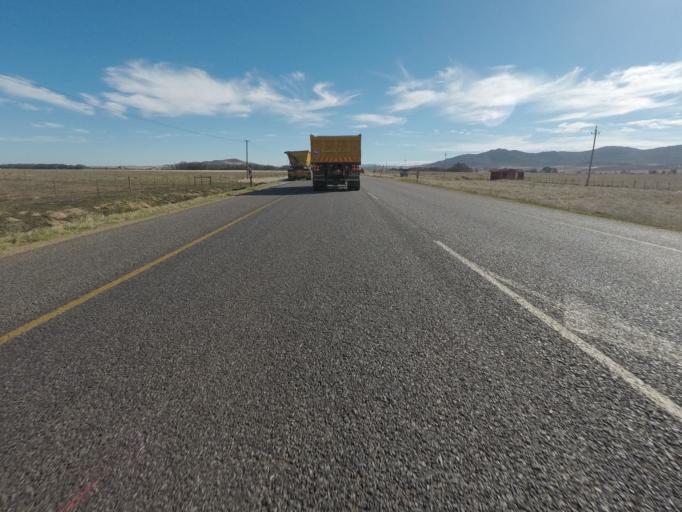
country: ZA
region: Western Cape
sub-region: West Coast District Municipality
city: Malmesbury
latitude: -33.6279
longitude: 18.7234
